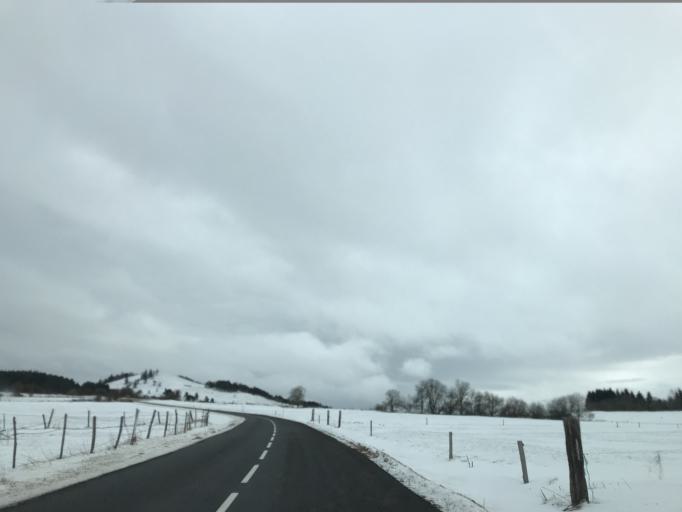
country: FR
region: Auvergne
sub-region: Departement du Puy-de-Dome
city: Aydat
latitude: 45.6757
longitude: 2.9342
